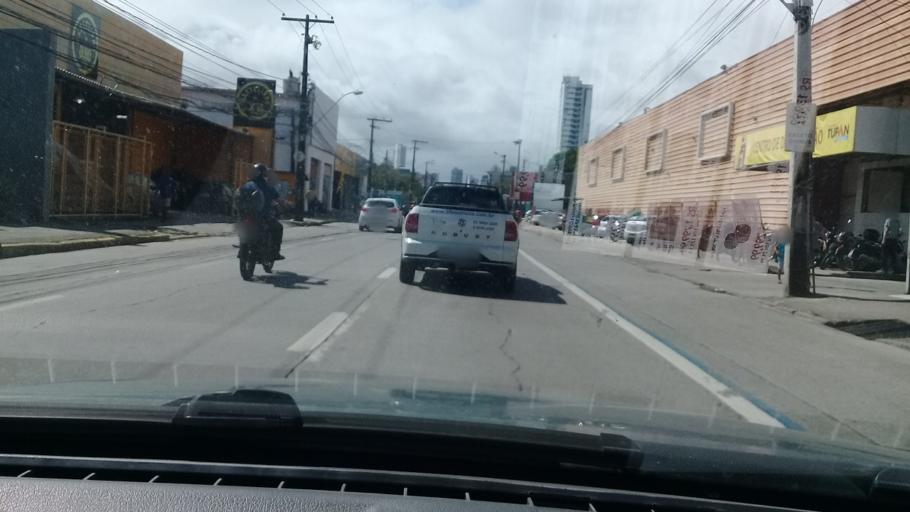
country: BR
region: Pernambuco
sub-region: Recife
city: Recife
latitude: -8.0679
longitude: -34.9084
